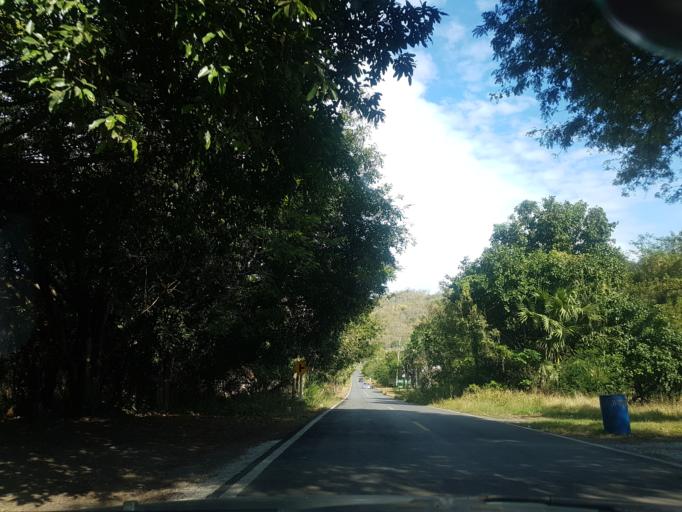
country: TH
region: Lop Buri
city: Lop Buri
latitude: 14.8185
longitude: 100.7510
